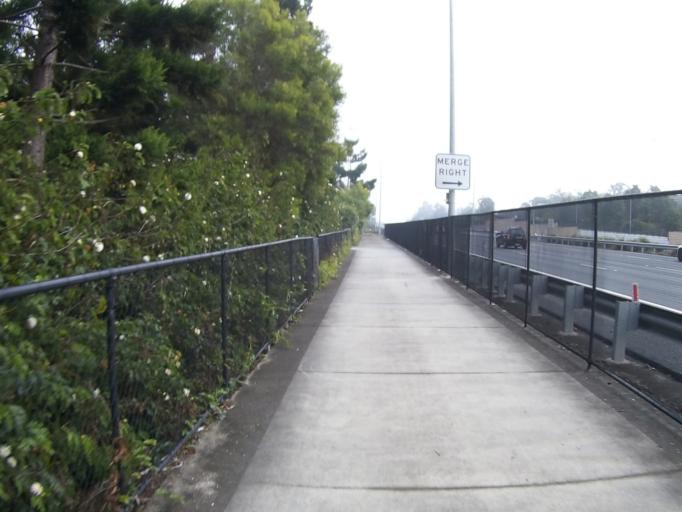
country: AU
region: Queensland
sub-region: Brisbane
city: Nathan
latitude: -27.5509
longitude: 153.0671
